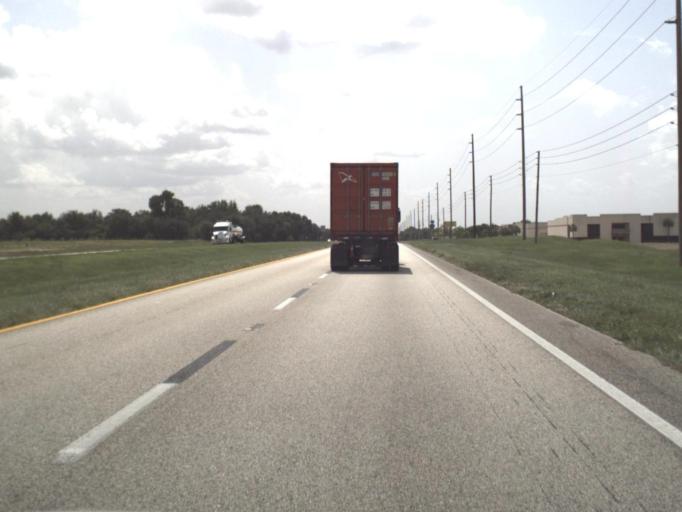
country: US
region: Florida
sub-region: Polk County
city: Lake Wales
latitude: 27.8759
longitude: -81.5959
